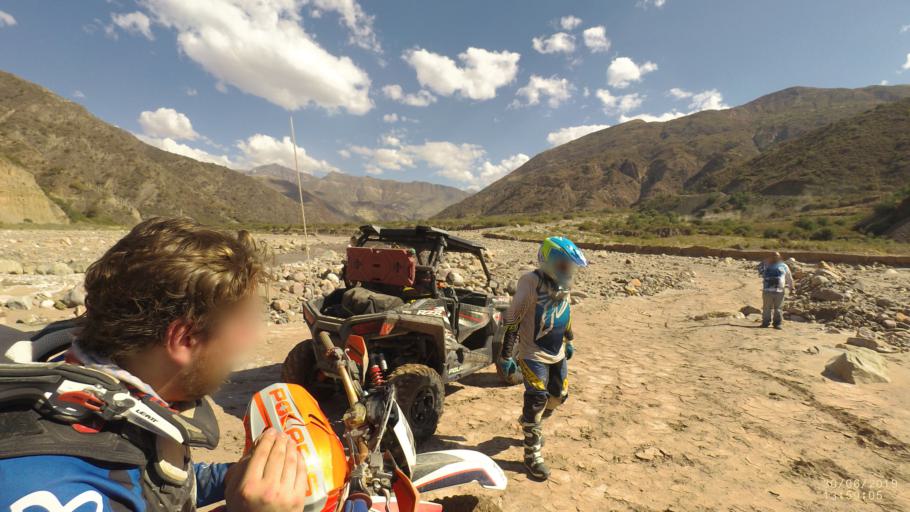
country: BO
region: Cochabamba
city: Irpa Irpa
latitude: -17.8051
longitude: -66.3568
